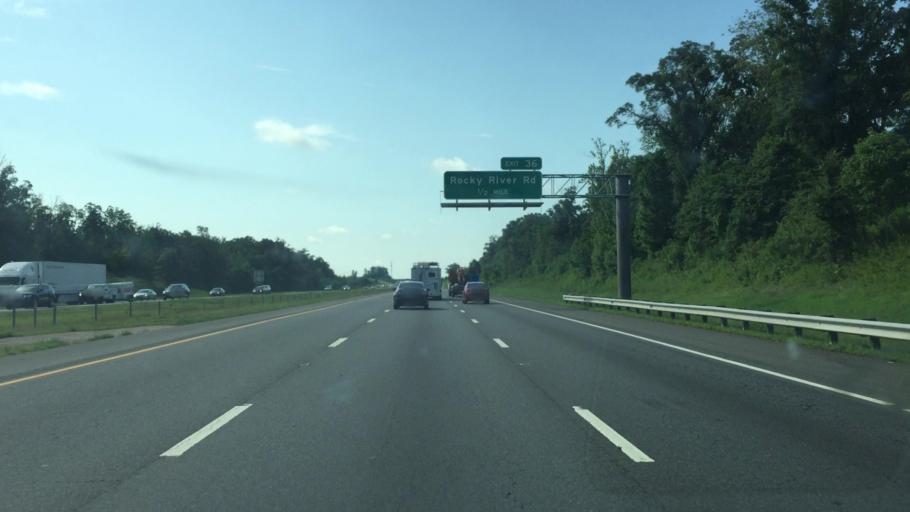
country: US
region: North Carolina
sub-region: Cabarrus County
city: Harrisburg
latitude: 35.2954
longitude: -80.6823
